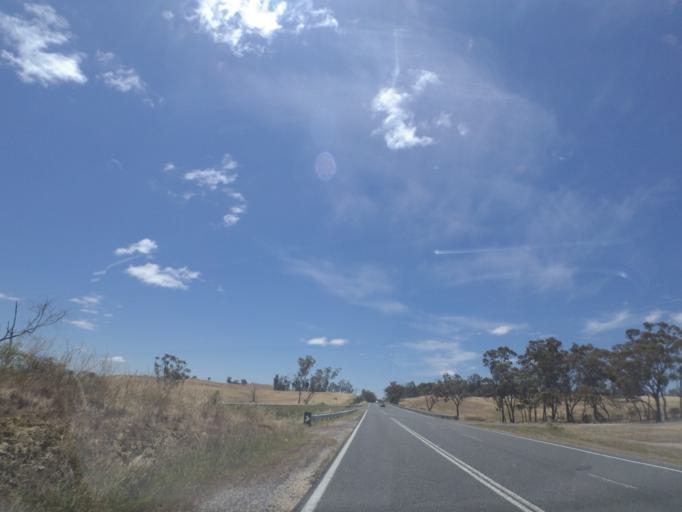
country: AU
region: Victoria
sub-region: Mount Alexander
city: Castlemaine
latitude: -37.2104
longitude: 144.1404
